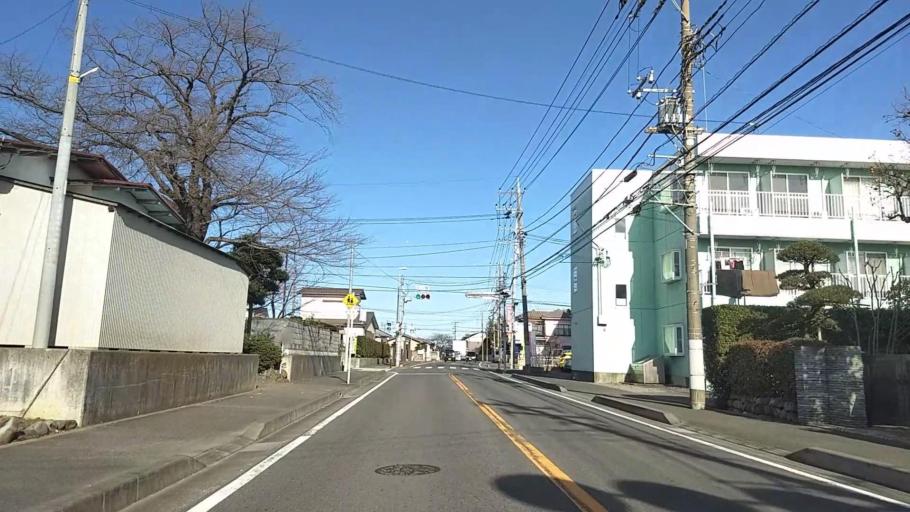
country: JP
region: Kanagawa
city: Atsugi
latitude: 35.4592
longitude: 139.3476
